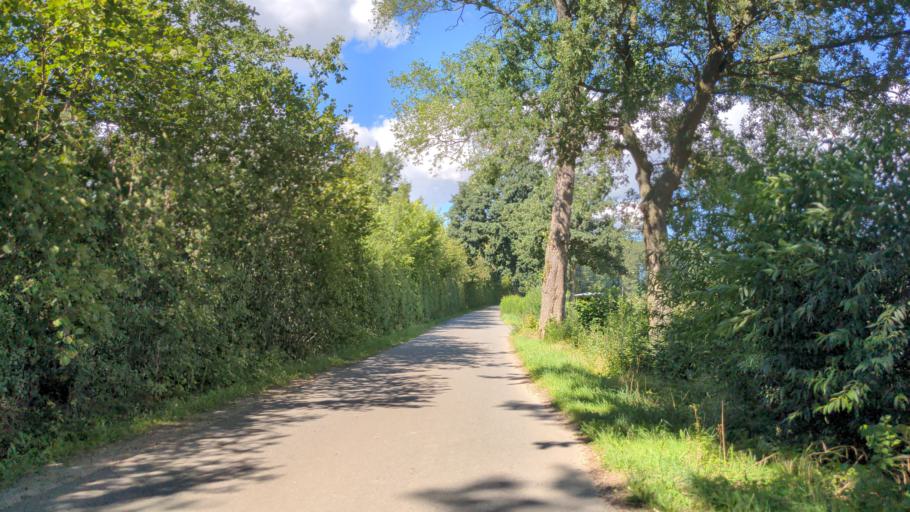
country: DE
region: Schleswig-Holstein
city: Beschendorf
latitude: 54.1724
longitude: 10.8606
